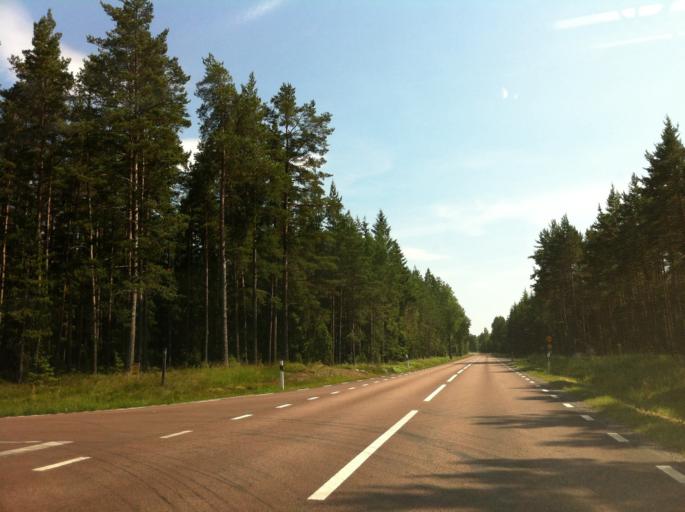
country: SE
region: Kalmar
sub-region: Nybro Kommun
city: Nybro
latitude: 56.8176
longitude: 15.7783
